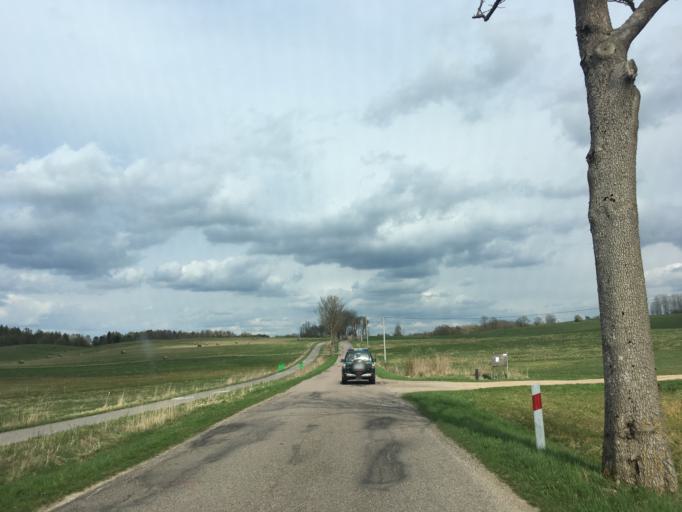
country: PL
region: Podlasie
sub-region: Powiat suwalski
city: Filipow
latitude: 54.3586
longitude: 22.7800
